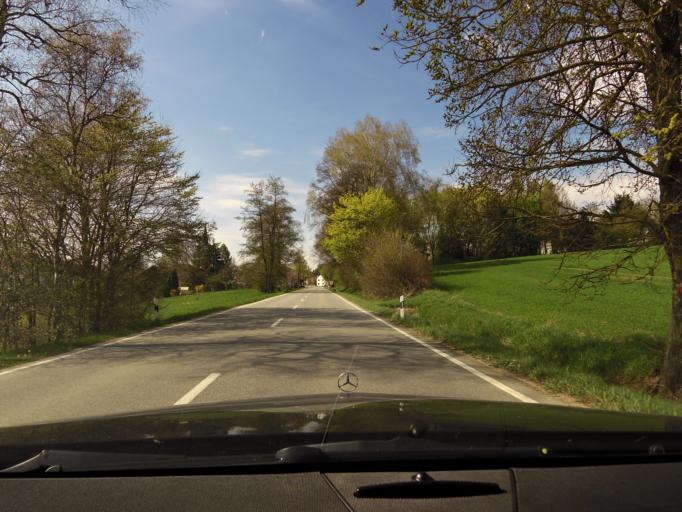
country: DE
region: Bavaria
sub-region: Lower Bavaria
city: Mallersdorf-Pfaffenberg
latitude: 48.7822
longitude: 12.1844
